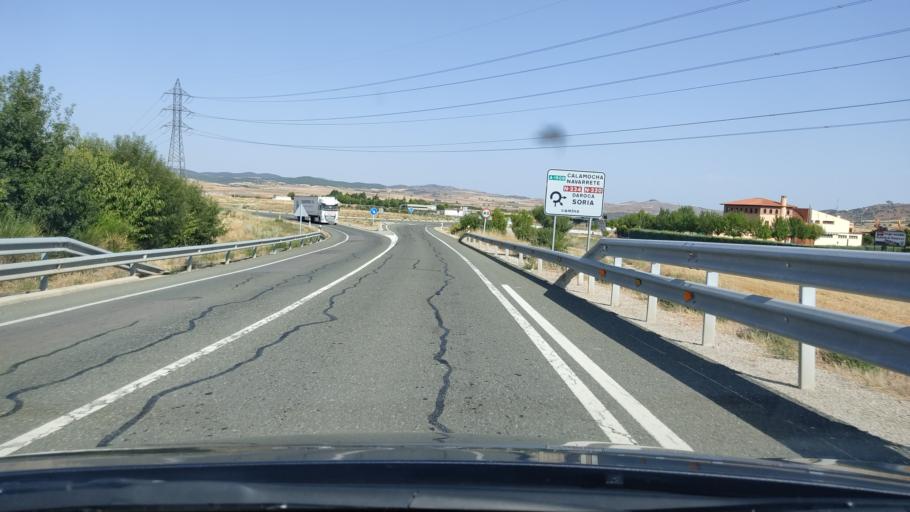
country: ES
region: Aragon
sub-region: Provincia de Teruel
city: Calamocha
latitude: 40.9154
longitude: -1.2823
